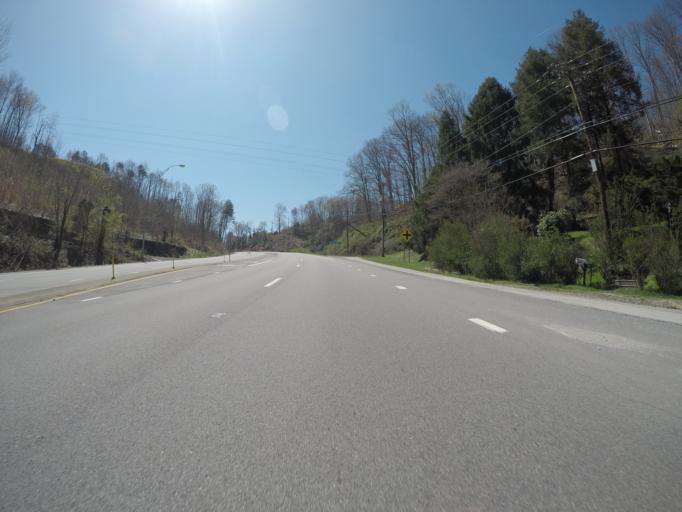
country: US
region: West Virginia
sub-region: Kanawha County
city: Charleston
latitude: 38.3512
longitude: -81.6025
